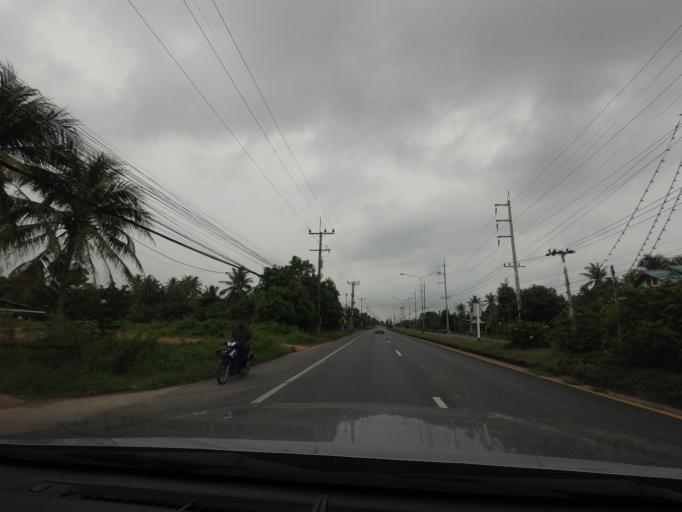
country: TH
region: Songkhla
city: Sathing Phra
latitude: 7.3870
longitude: 100.4700
